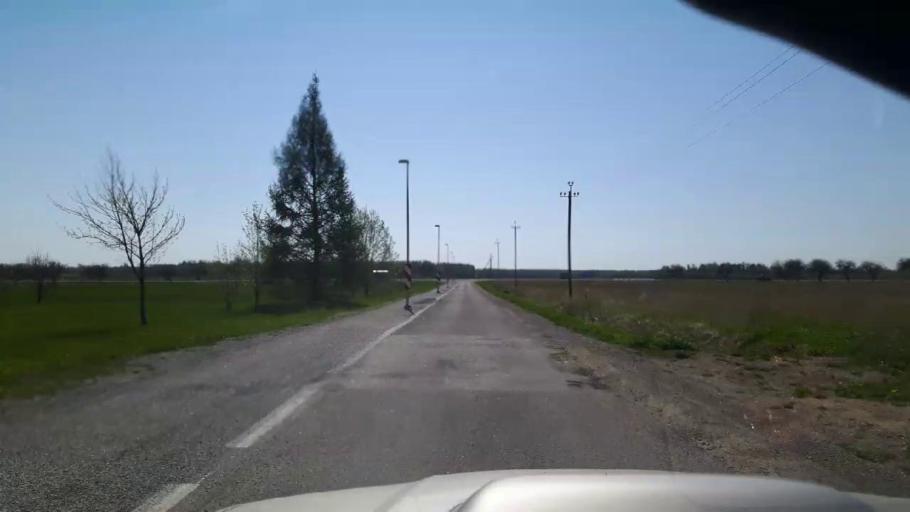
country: EE
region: Paernumaa
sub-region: Tootsi vald
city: Tootsi
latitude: 58.4757
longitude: 24.8018
